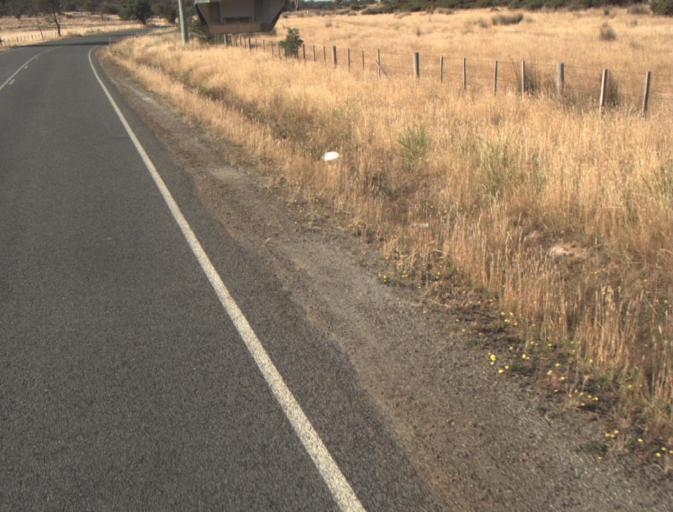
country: AU
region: Tasmania
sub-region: Launceston
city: Newstead
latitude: -41.4399
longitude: 147.2547
